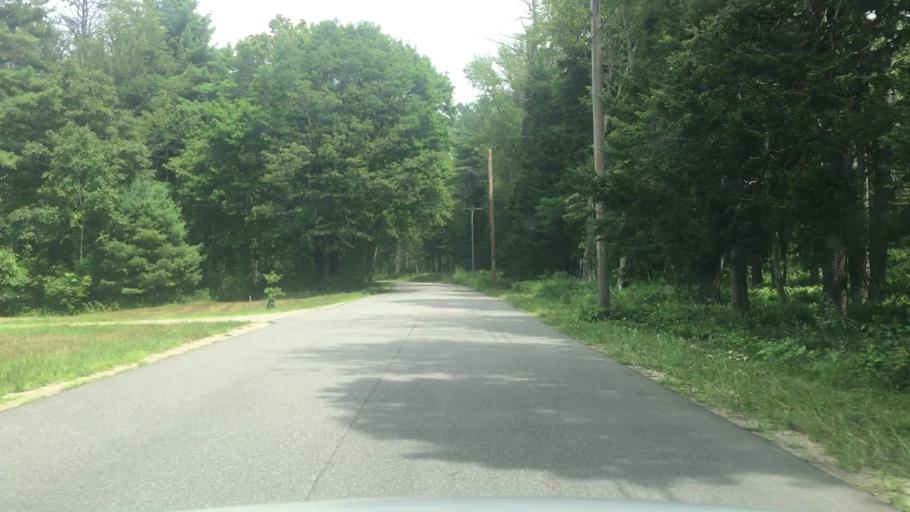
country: US
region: Maine
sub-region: Cumberland County
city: Scarborough
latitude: 43.5708
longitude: -70.2579
